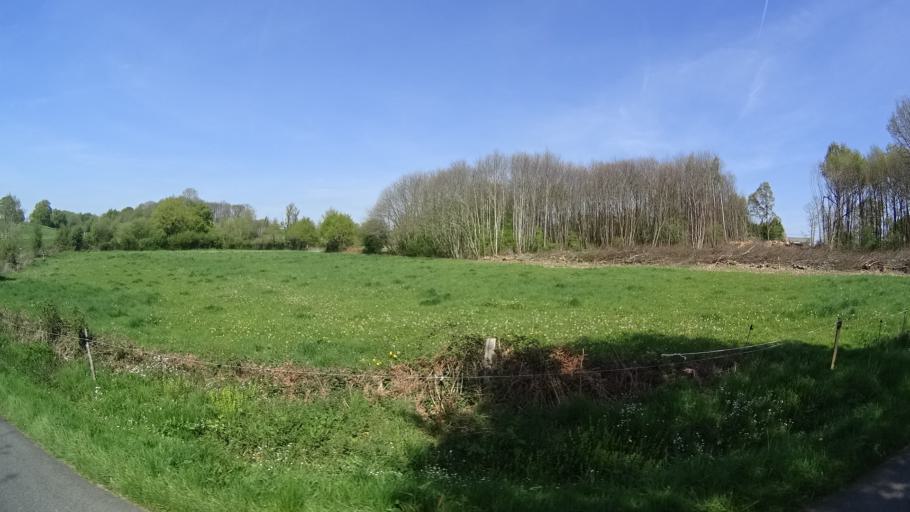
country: FR
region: Pays de la Loire
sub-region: Departement de la Loire-Atlantique
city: Fegreac
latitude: 47.5925
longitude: -2.0488
